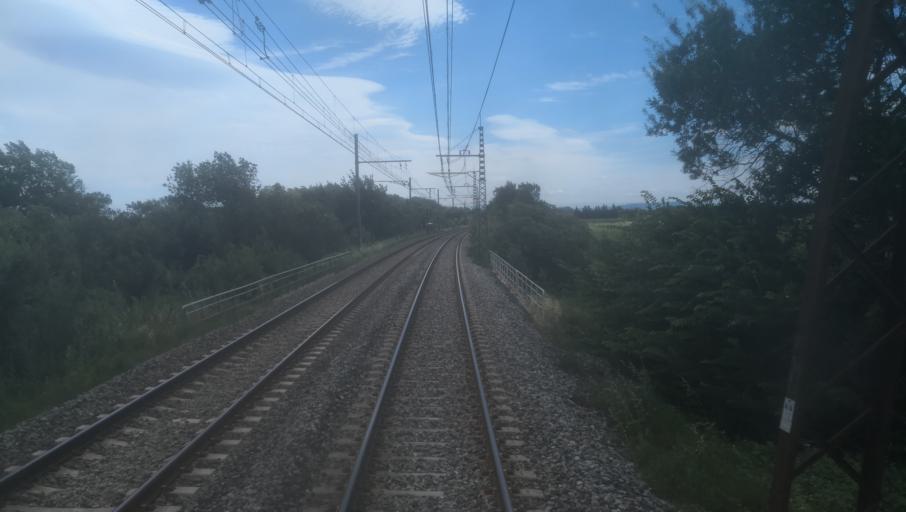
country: FR
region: Languedoc-Roussillon
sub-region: Departement de l'Aude
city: Coursan
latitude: 43.2497
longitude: 3.0673
